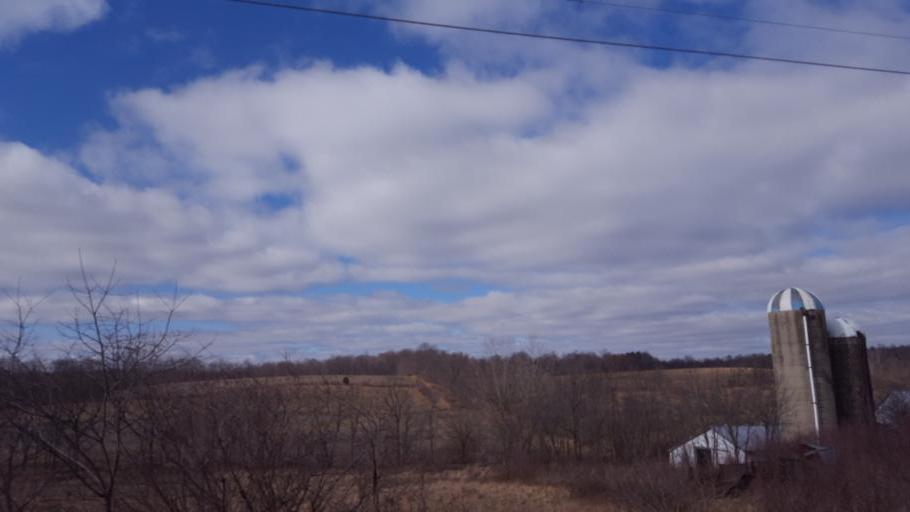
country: US
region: Ohio
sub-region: Sandusky County
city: Bellville
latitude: 40.5611
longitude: -82.5094
